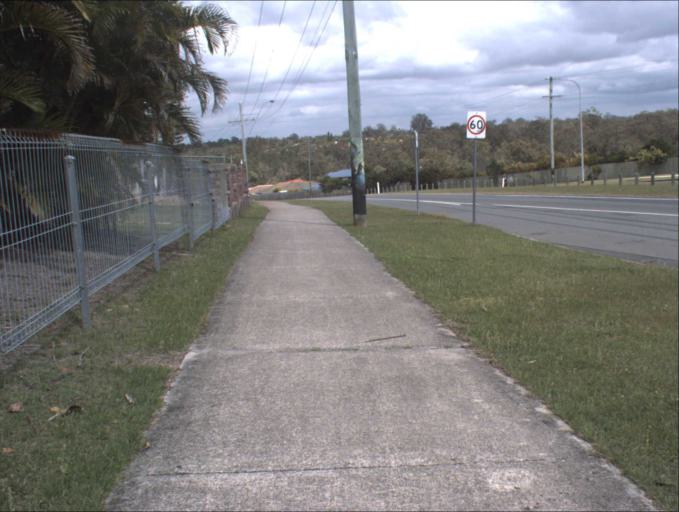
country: AU
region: Queensland
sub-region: Logan
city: Logan Reserve
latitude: -27.6826
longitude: 153.0596
